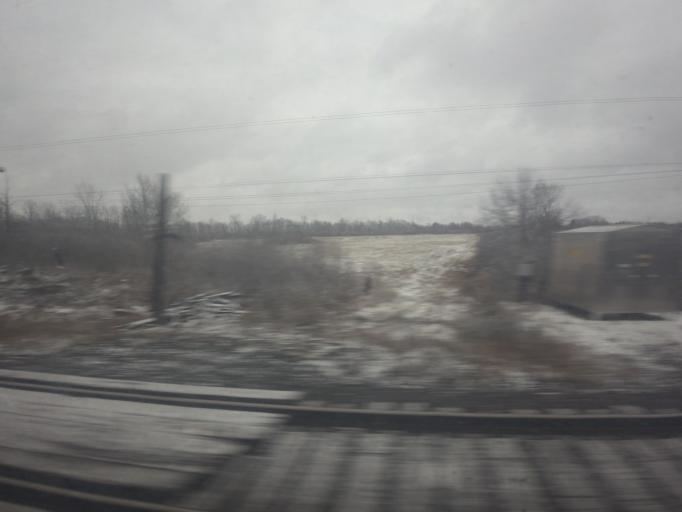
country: US
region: New York
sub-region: Jefferson County
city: Alexandria Bay
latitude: 44.4103
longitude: -76.0060
